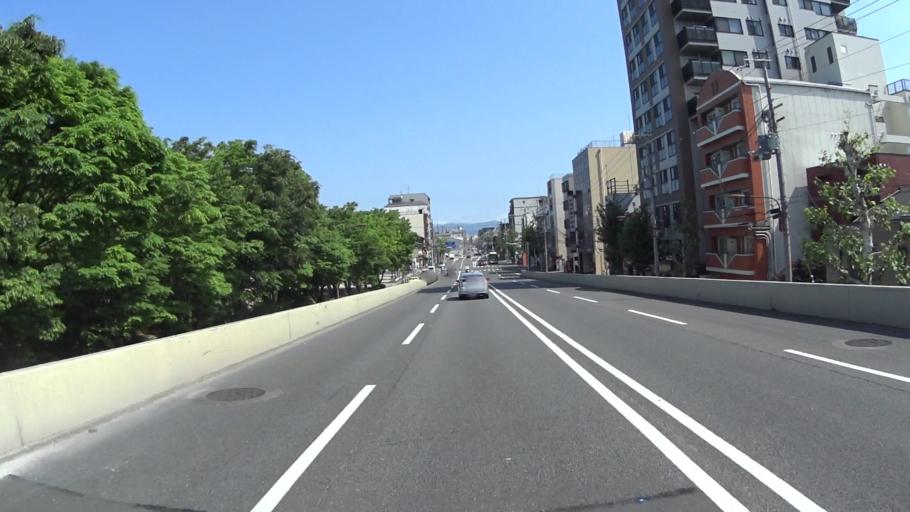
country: JP
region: Kyoto
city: Kyoto
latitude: 34.9867
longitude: 135.7492
